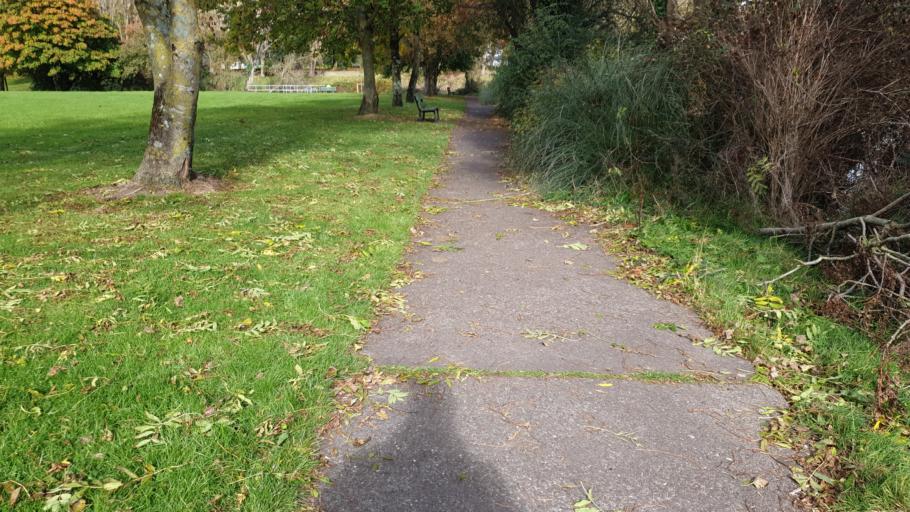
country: IE
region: Munster
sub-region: County Cork
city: Cork
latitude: 51.8996
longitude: -8.4328
